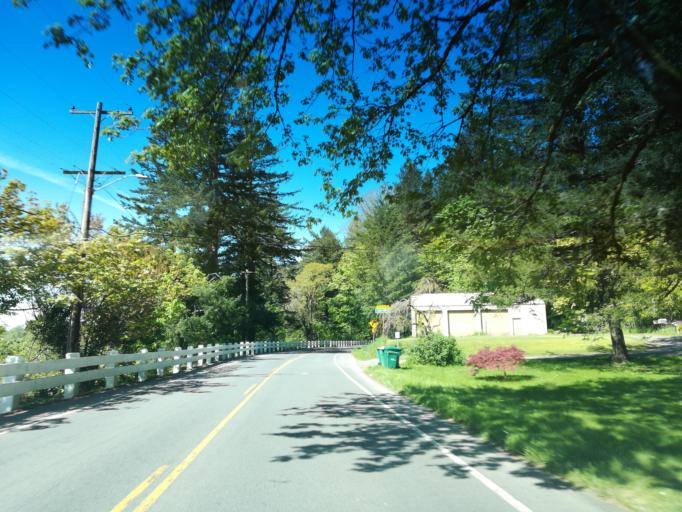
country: US
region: Oregon
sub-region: Multnomah County
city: Troutdale
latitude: 45.5317
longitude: -122.3718
